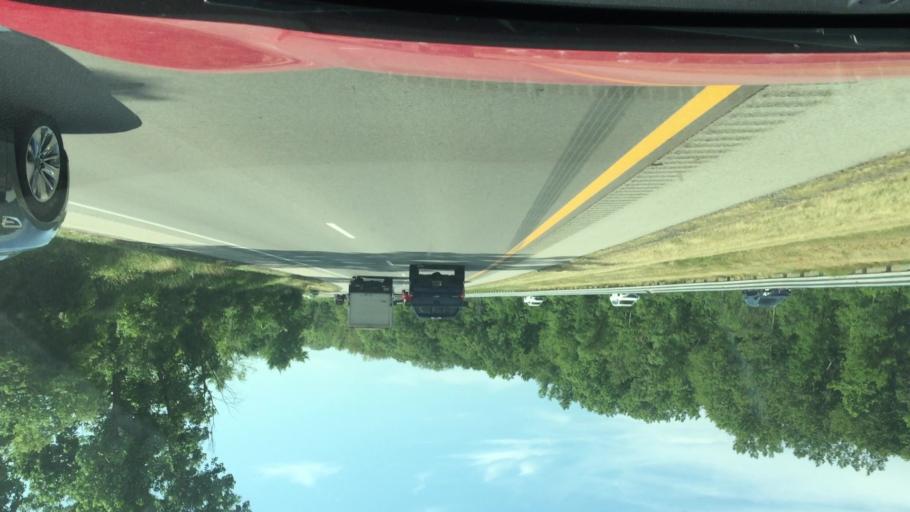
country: US
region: Michigan
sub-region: Washtenaw County
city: Milan
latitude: 42.0444
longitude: -83.6699
